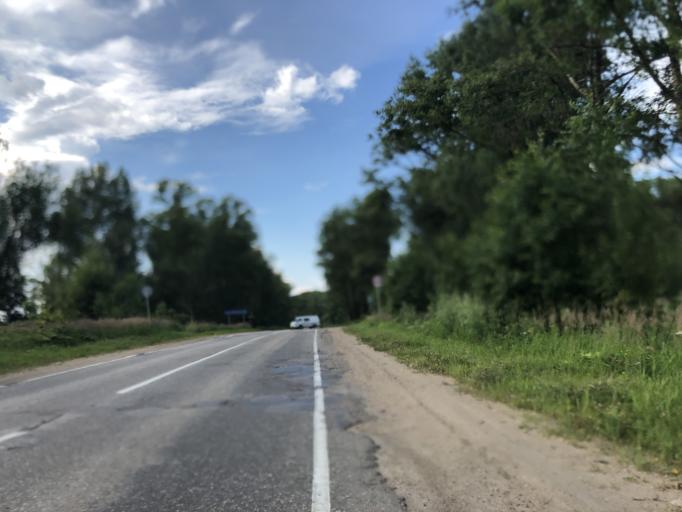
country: RU
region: Tverskaya
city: Rzhev
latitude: 56.2649
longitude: 34.2513
